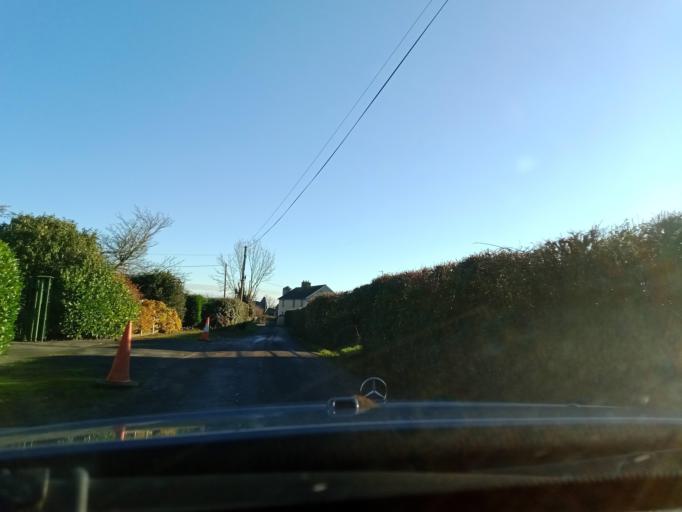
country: IE
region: Leinster
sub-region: Kilkenny
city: Mooncoin
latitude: 52.2897
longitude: -7.2099
